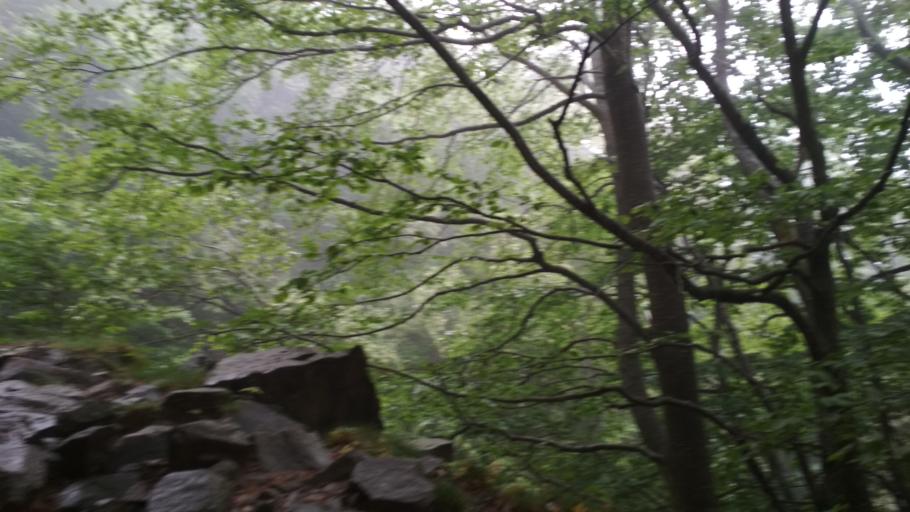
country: ES
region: Catalonia
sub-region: Provincia de Barcelona
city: Fogars de Montclus
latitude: 41.7743
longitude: 2.4412
